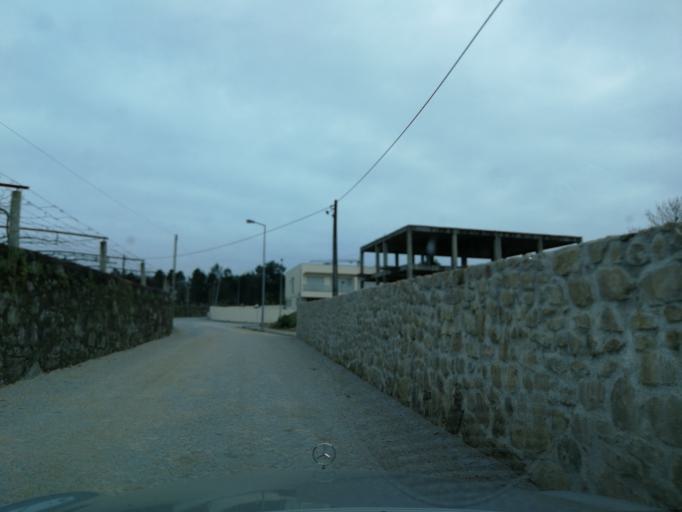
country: PT
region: Braga
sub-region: Braga
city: Braga
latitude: 41.5772
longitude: -8.4418
